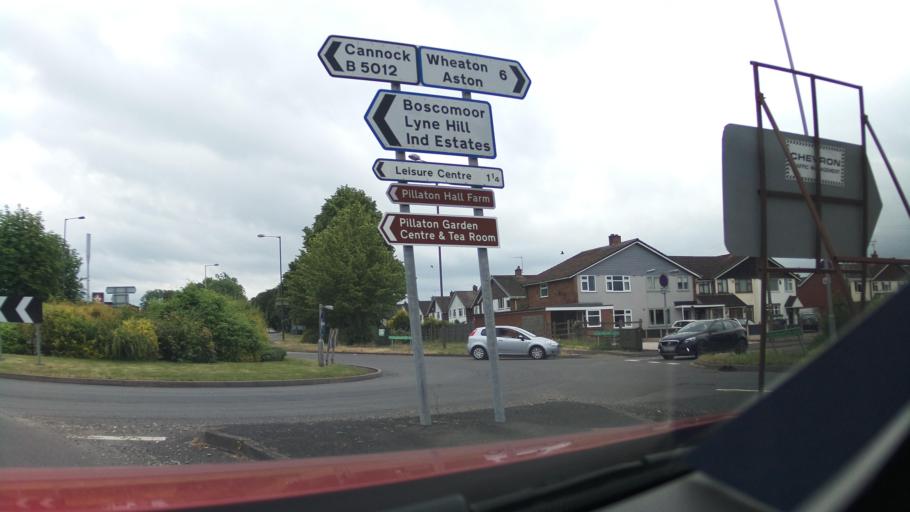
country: GB
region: England
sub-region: Staffordshire
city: Penkridge
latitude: 52.7184
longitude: -2.1179
